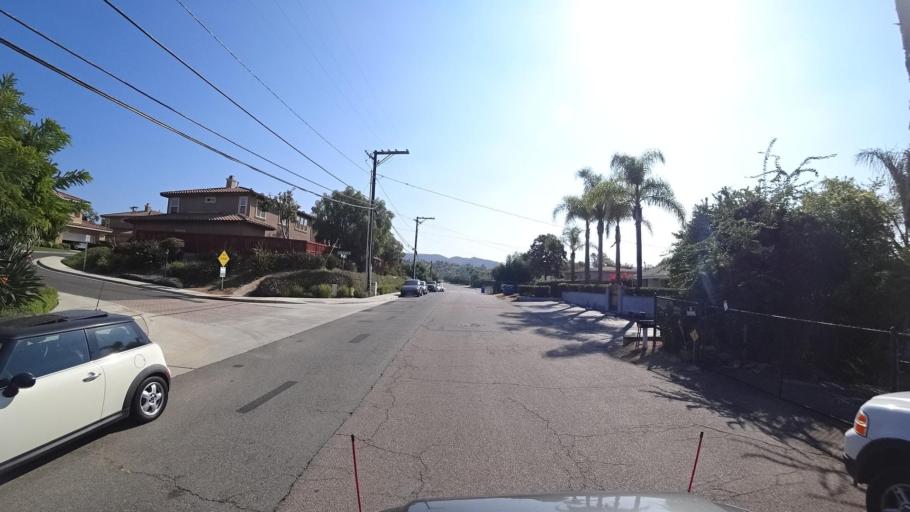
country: US
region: California
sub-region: San Diego County
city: Vista
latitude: 33.1756
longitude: -117.2156
